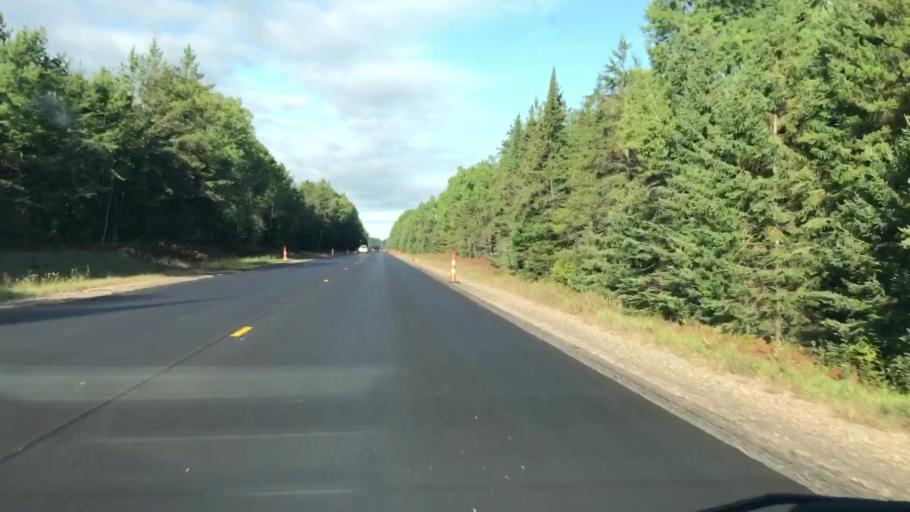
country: US
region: Michigan
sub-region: Mackinac County
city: Saint Ignace
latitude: 46.3459
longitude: -84.9317
